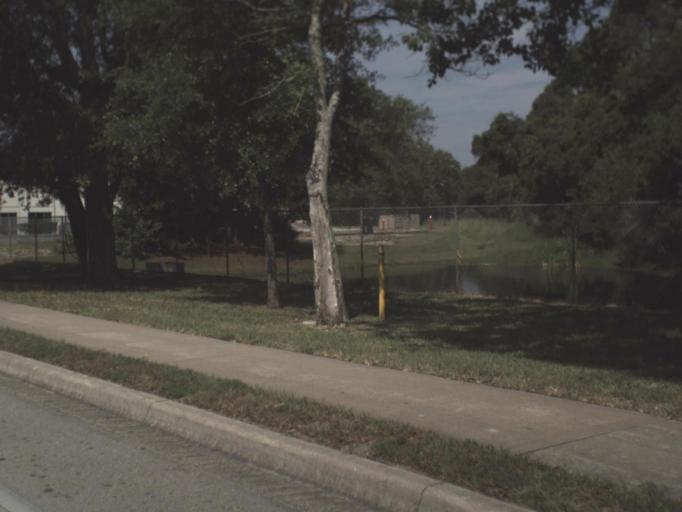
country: US
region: Florida
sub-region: Saint Johns County
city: Saint Augustine South
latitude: 29.8657
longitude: -81.3420
